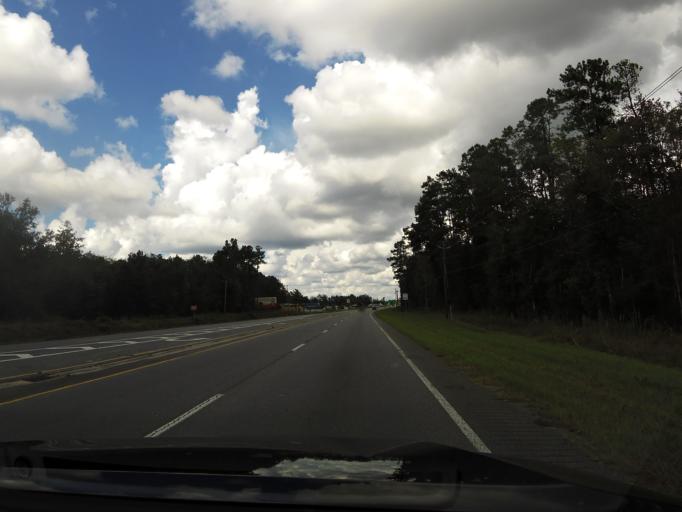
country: US
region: Georgia
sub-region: Charlton County
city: Folkston
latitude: 30.8522
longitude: -82.0094
